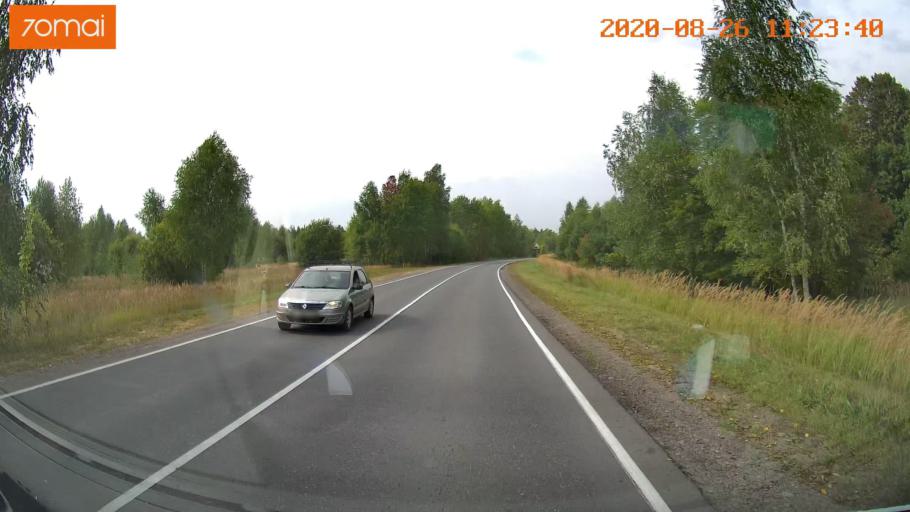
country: RU
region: Rjazan
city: Shilovo
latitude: 54.3502
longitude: 41.0062
